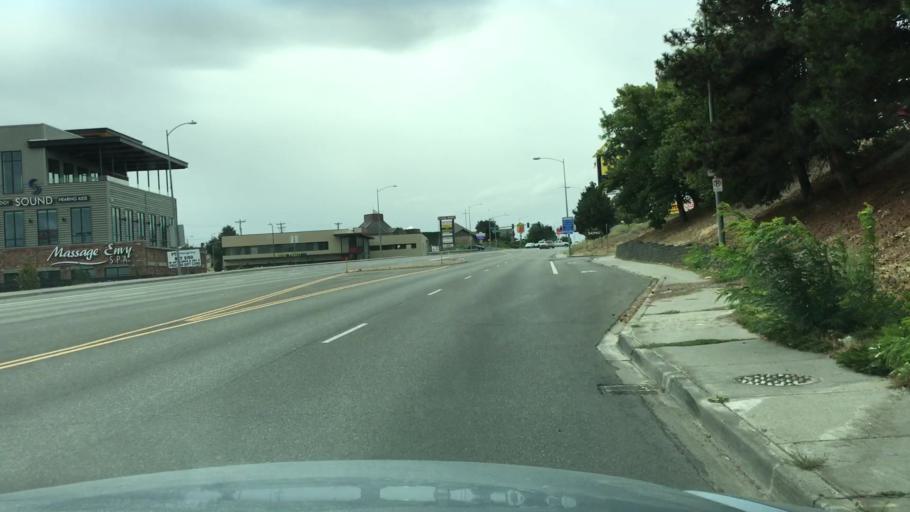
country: US
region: Washington
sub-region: Franklin County
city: West Pasco
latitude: 46.2205
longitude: -119.2241
